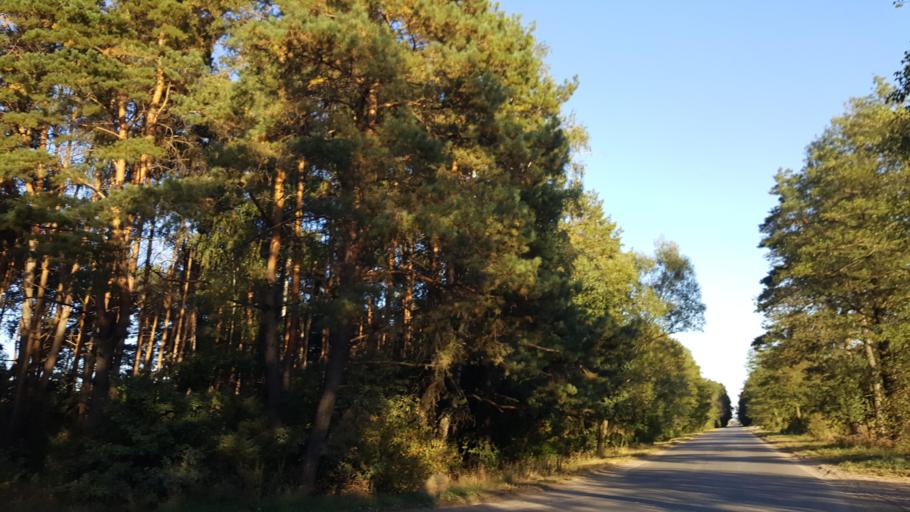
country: BY
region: Brest
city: Vysokaye
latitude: 52.3071
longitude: 23.4607
